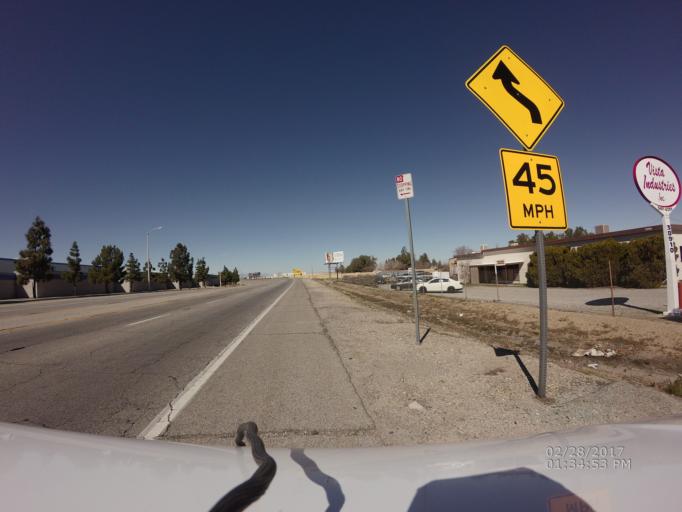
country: US
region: California
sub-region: Los Angeles County
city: Palmdale
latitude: 34.5896
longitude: -118.1180
